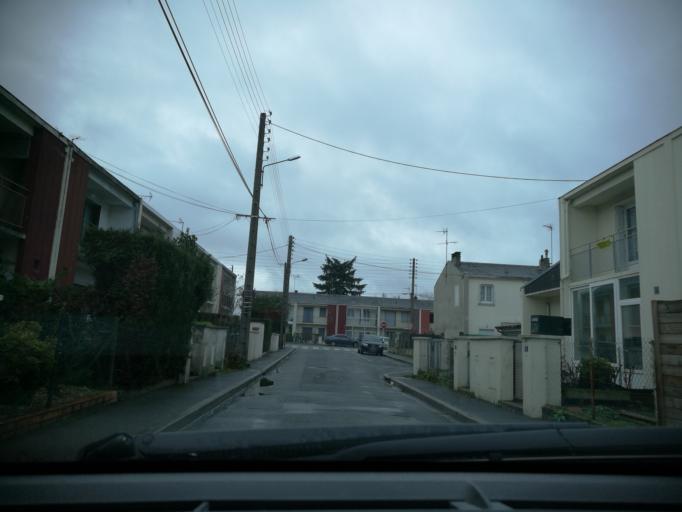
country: FR
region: Centre
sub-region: Departement du Loiret
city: Fleury-les-Aubrais
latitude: 47.9349
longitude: 1.9127
